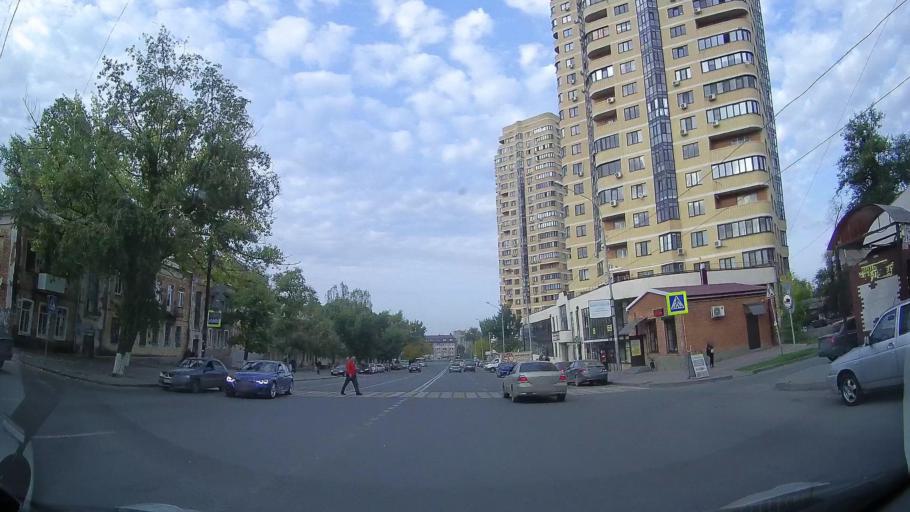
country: RU
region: Rostov
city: Rostov-na-Donu
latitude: 47.2420
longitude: 39.7018
